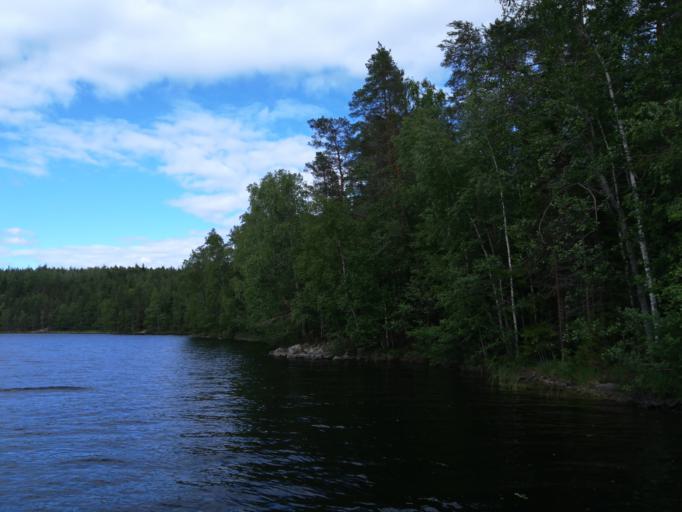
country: FI
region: South Karelia
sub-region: Lappeenranta
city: Savitaipale
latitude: 61.3041
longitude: 27.6113
